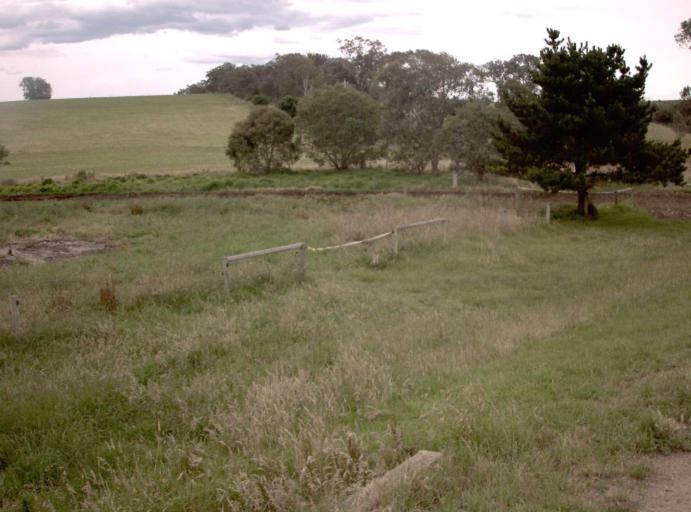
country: AU
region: Victoria
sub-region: East Gippsland
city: Bairnsdale
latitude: -37.7681
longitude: 147.3219
